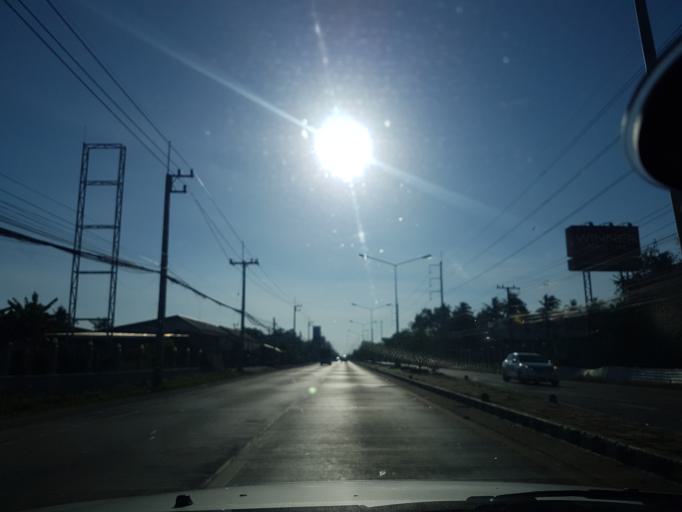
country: TH
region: Lop Buri
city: Lop Buri
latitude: 14.7689
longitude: 100.7066
